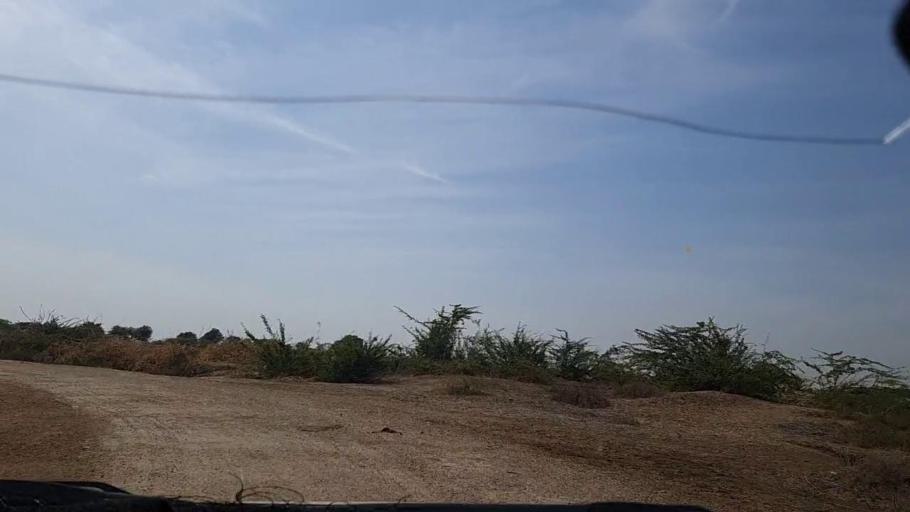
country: PK
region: Sindh
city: Pithoro
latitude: 25.4826
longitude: 69.4362
